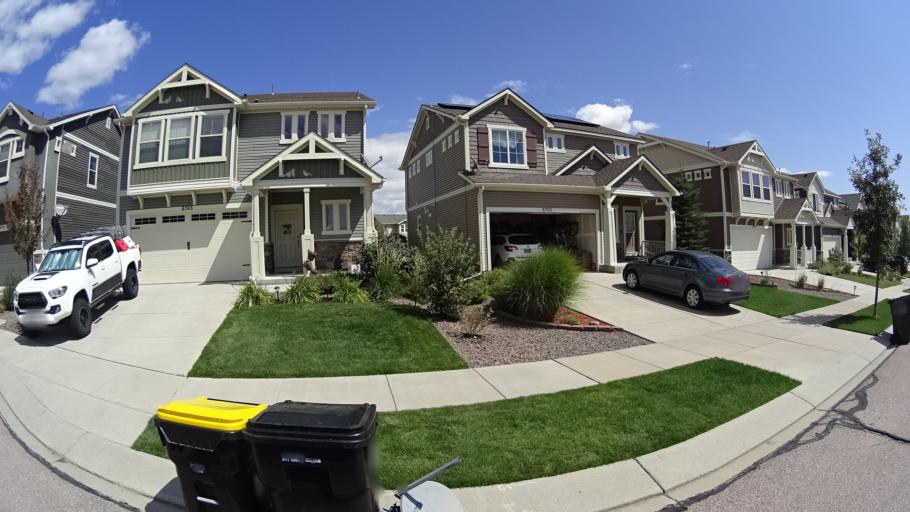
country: US
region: Colorado
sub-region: El Paso County
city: Cimarron Hills
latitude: 38.9296
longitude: -104.6738
